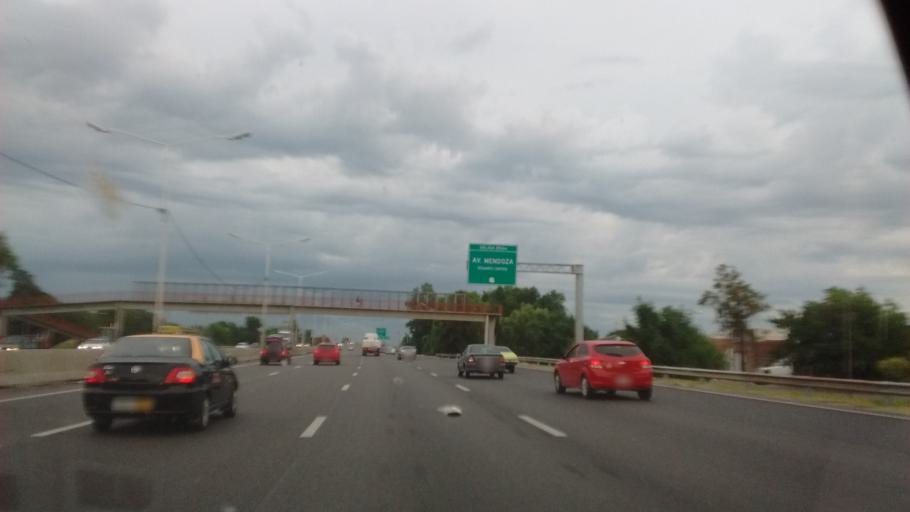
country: AR
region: Santa Fe
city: Perez
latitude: -32.9463
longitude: -60.7220
